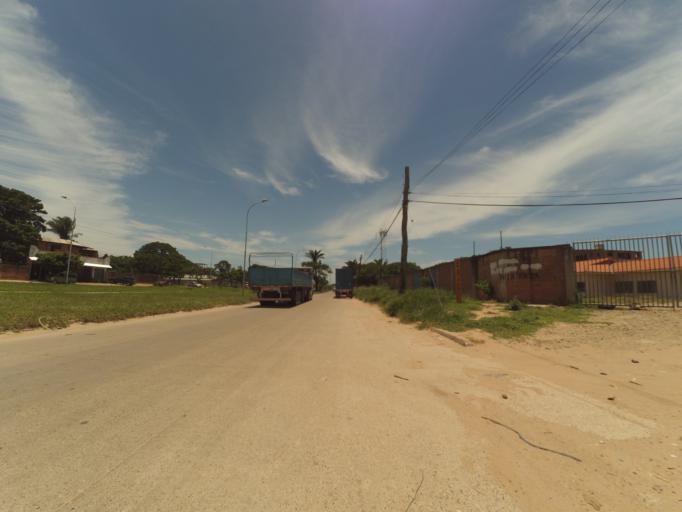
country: BO
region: Santa Cruz
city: Santa Cruz de la Sierra
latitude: -17.8089
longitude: -63.2226
